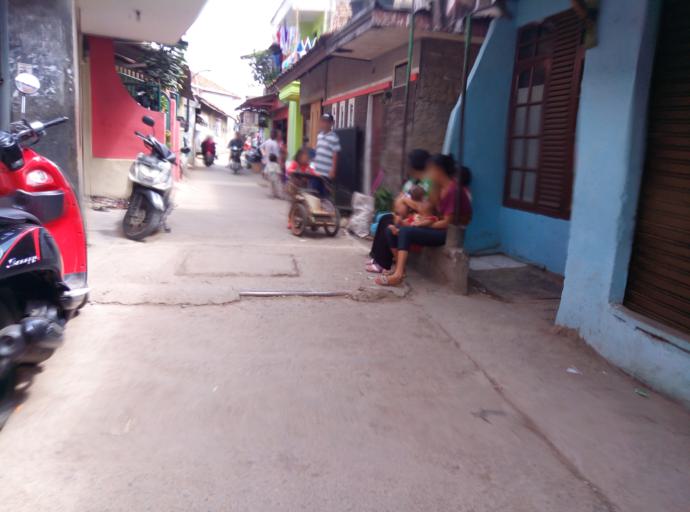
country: ID
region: West Java
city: Bandung
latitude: -6.9276
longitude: 107.6527
